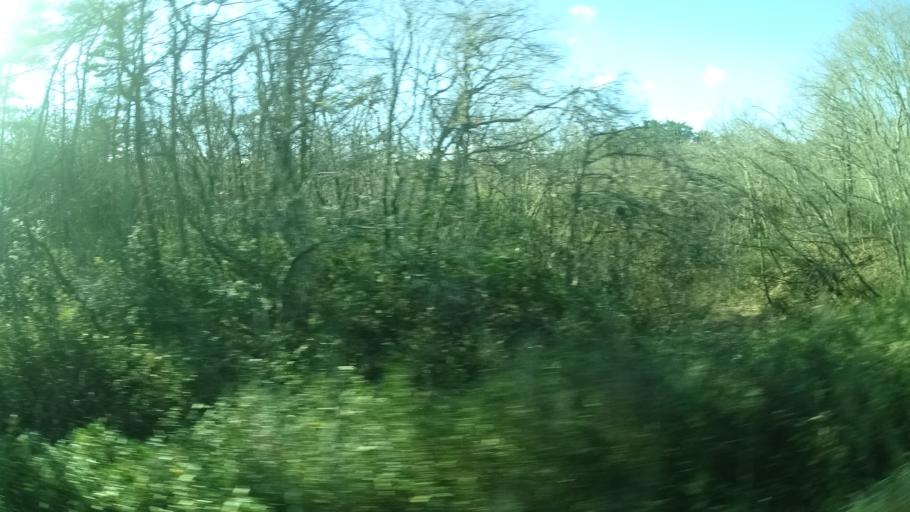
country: JP
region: Miyagi
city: Marumori
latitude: 37.7364
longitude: 140.9495
